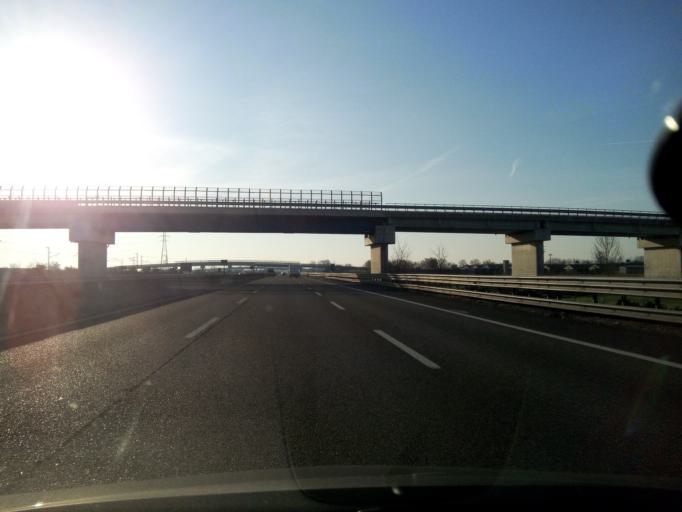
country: IT
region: Emilia-Romagna
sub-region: Provincia di Piacenza
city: Fiorenzuola d'Arda
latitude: 44.9448
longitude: 9.9471
